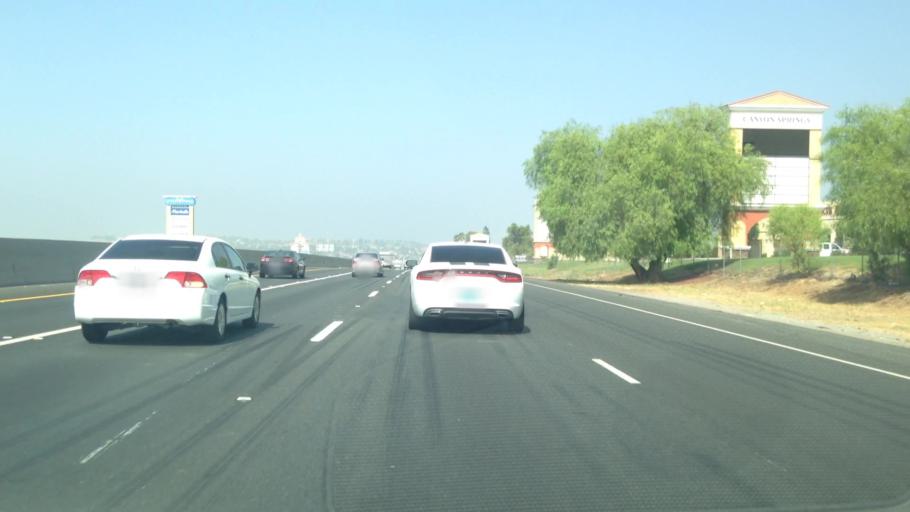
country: US
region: California
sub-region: Riverside County
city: Moreno Valley
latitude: 33.9383
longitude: -117.2771
